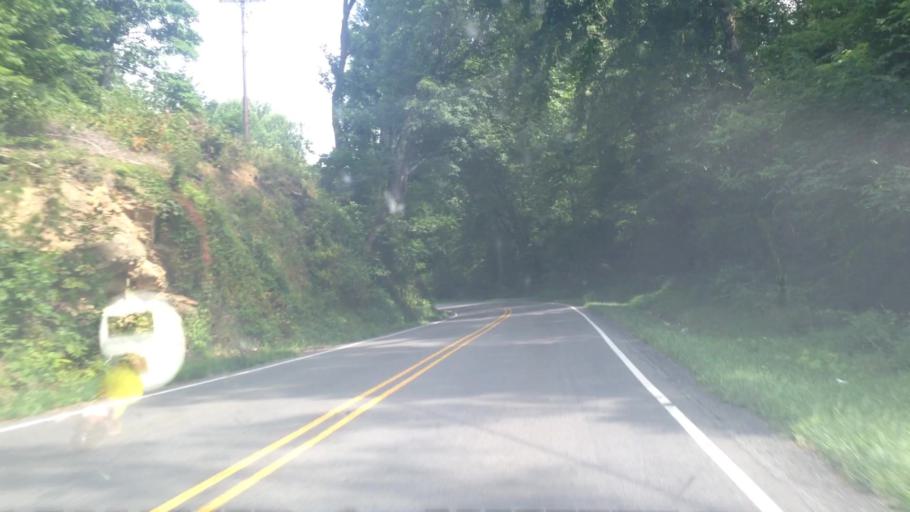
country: US
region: North Carolina
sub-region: Surry County
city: Mount Airy
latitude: 36.4810
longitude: -80.5810
